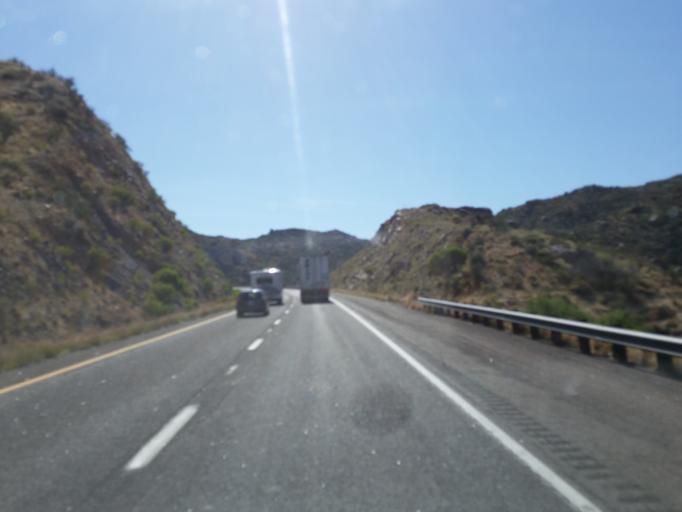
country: US
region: Arizona
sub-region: Mohave County
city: Peach Springs
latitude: 35.1705
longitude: -113.5162
